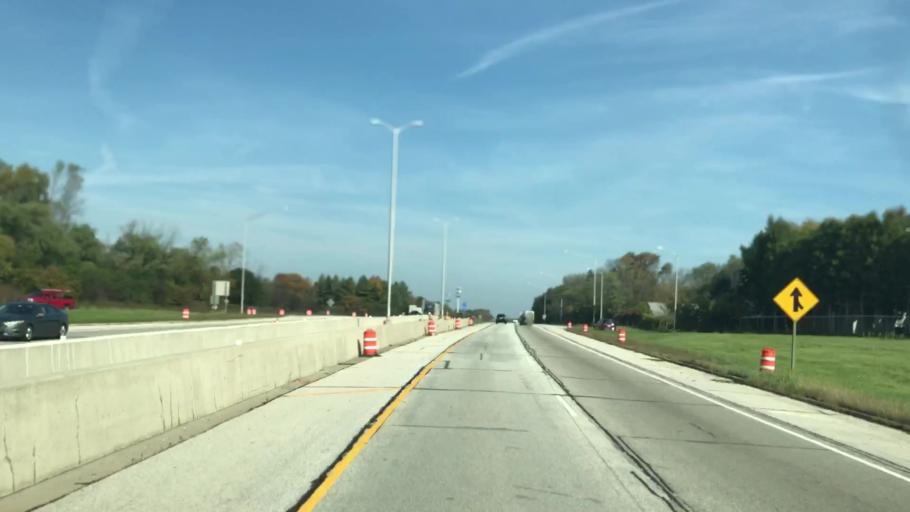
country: US
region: Wisconsin
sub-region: Milwaukee County
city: Fox Point
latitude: 43.1486
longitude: -87.9159
